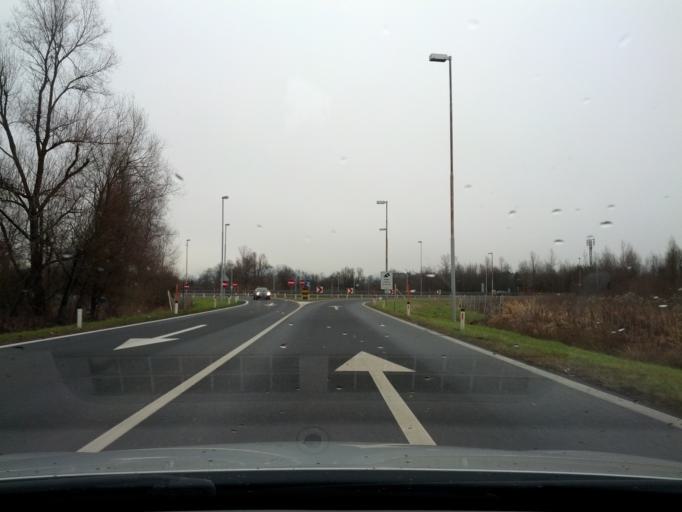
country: SI
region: Ljubljana
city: Ljubljana
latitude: 46.0242
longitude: 14.4968
